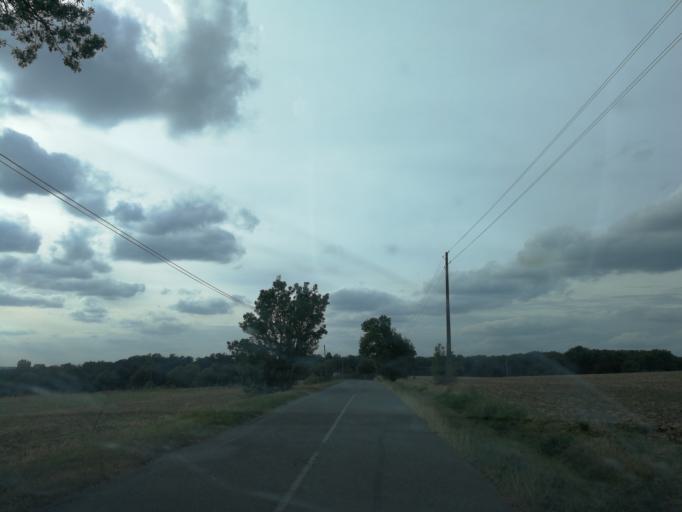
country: FR
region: Midi-Pyrenees
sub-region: Departement de la Haute-Garonne
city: Flourens
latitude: 43.6029
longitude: 1.5388
